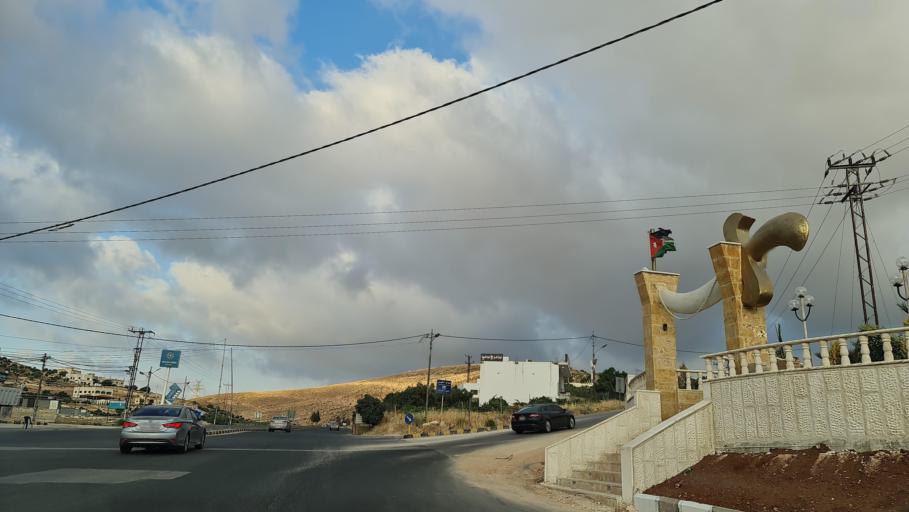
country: JO
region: Amman
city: Al Jubayhah
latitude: 32.0913
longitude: 35.9361
